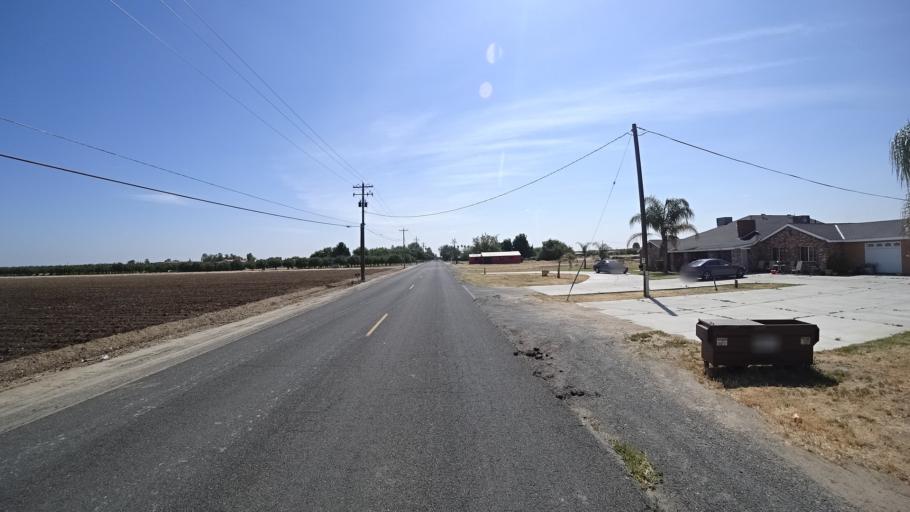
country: US
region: California
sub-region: Kings County
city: Lemoore
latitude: 36.2692
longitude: -119.7708
